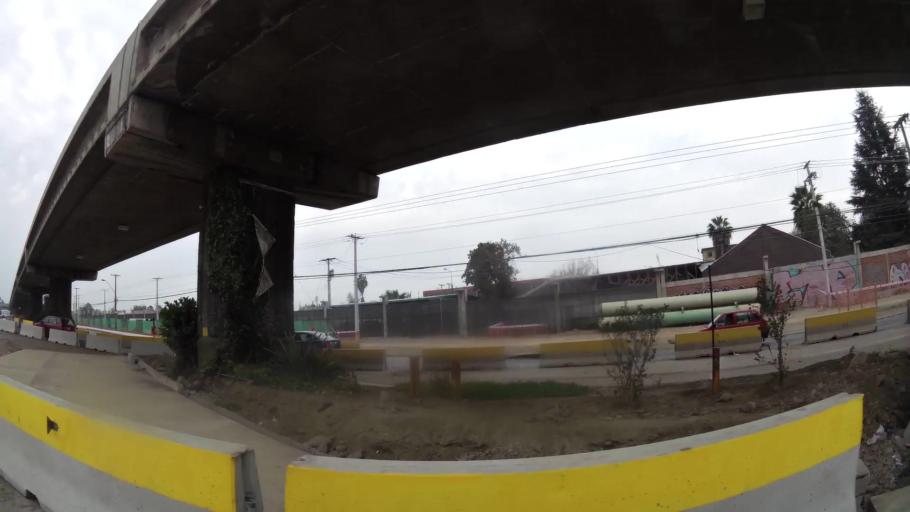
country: CL
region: Santiago Metropolitan
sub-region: Provincia de Santiago
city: Villa Presidente Frei, Nunoa, Santiago, Chile
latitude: -33.5020
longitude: -70.6153
